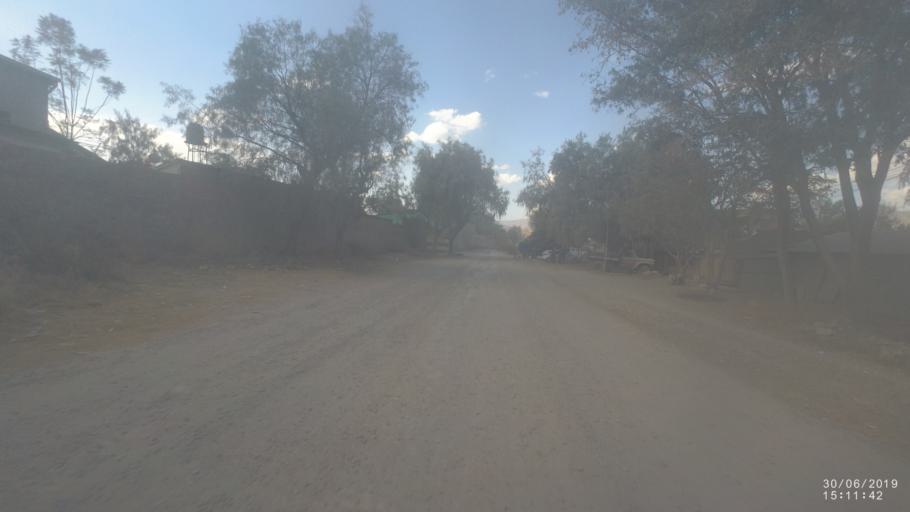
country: BO
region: Cochabamba
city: Irpa Irpa
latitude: -17.7268
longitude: -66.2905
